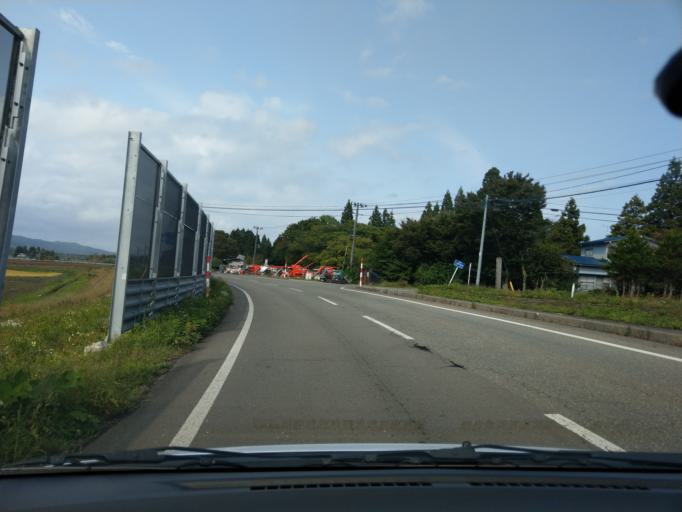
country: JP
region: Akita
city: Omagari
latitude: 39.5279
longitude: 140.2628
